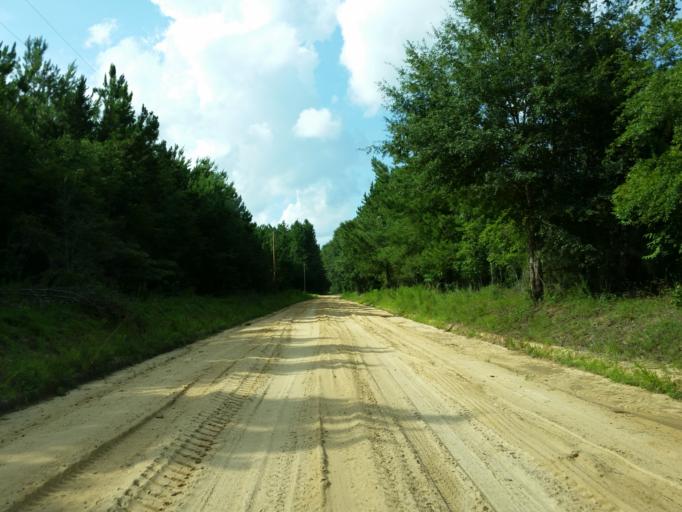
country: US
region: Georgia
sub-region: Lee County
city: Leesburg
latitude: 31.7669
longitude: -84.0185
